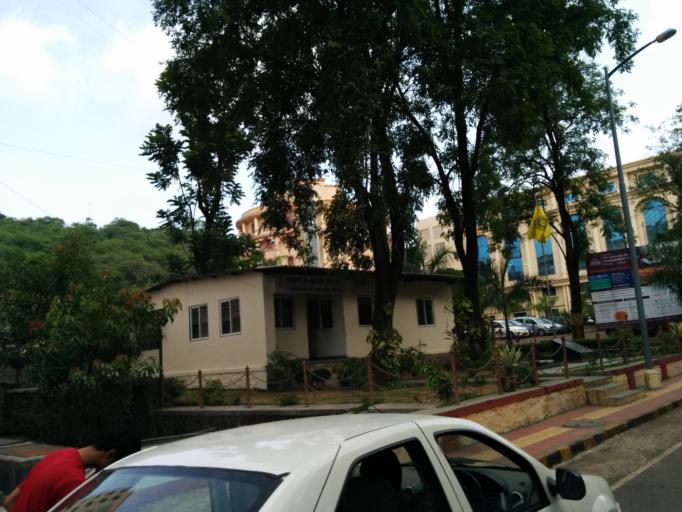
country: IN
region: Maharashtra
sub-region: Pune Division
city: Shivaji Nagar
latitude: 18.5161
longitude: 73.8154
